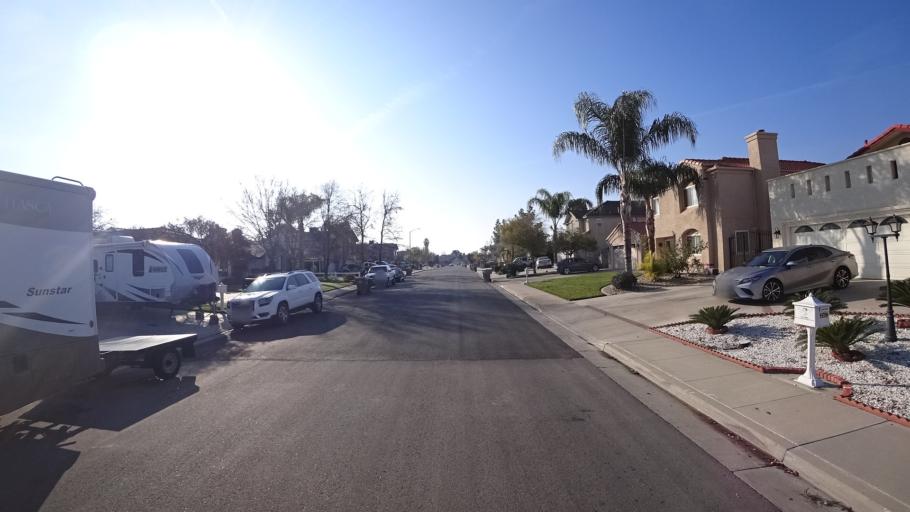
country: US
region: California
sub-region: Kern County
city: Oildale
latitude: 35.4058
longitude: -118.9344
